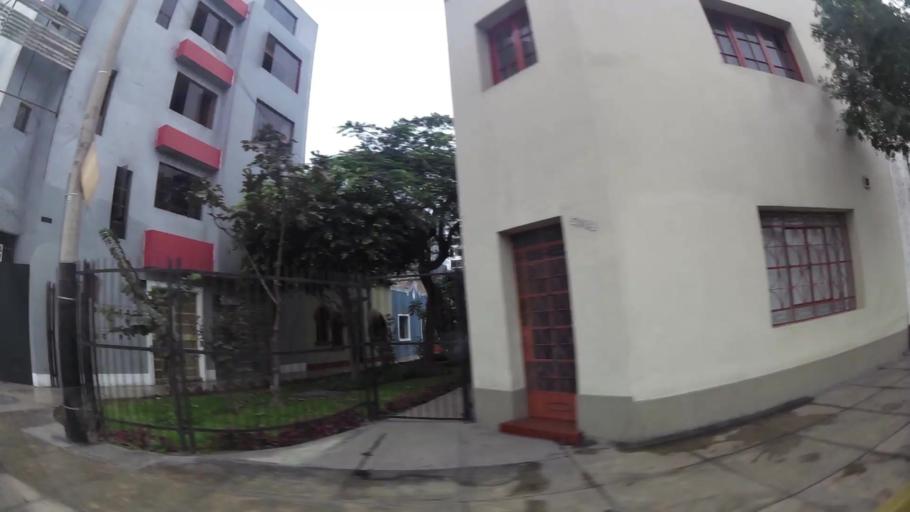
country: PE
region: Lima
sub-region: Lima
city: Surco
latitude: -12.1230
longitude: -77.0250
